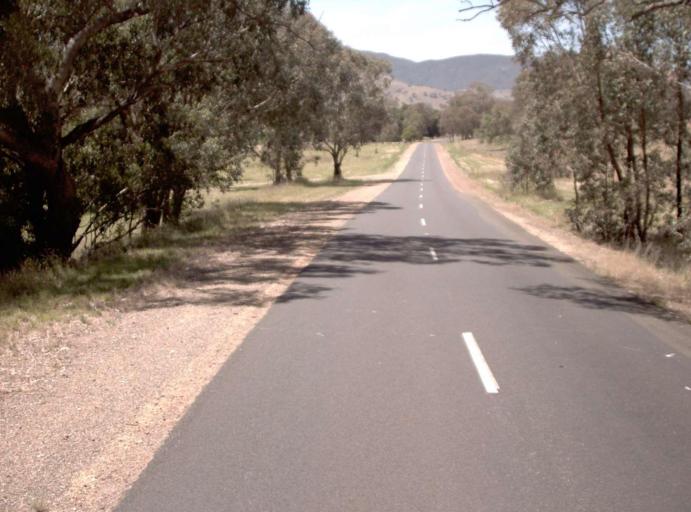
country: AU
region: Victoria
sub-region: East Gippsland
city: Bairnsdale
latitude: -37.1766
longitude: 147.7023
